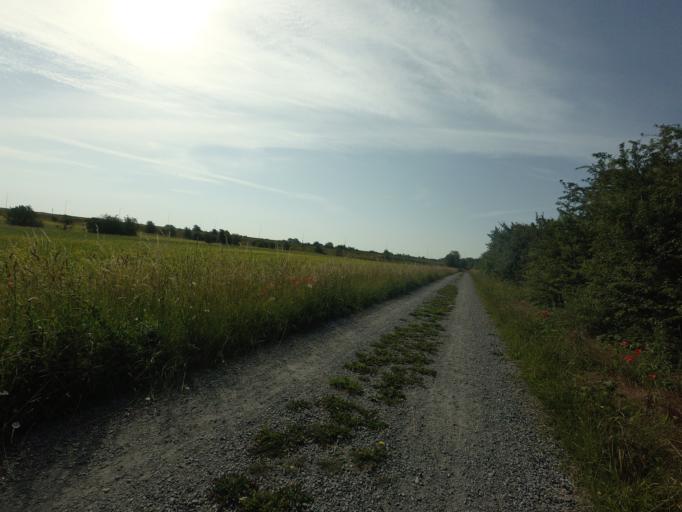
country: SE
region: Skane
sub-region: Vellinge Kommun
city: Vellinge
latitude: 55.4854
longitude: 13.0160
